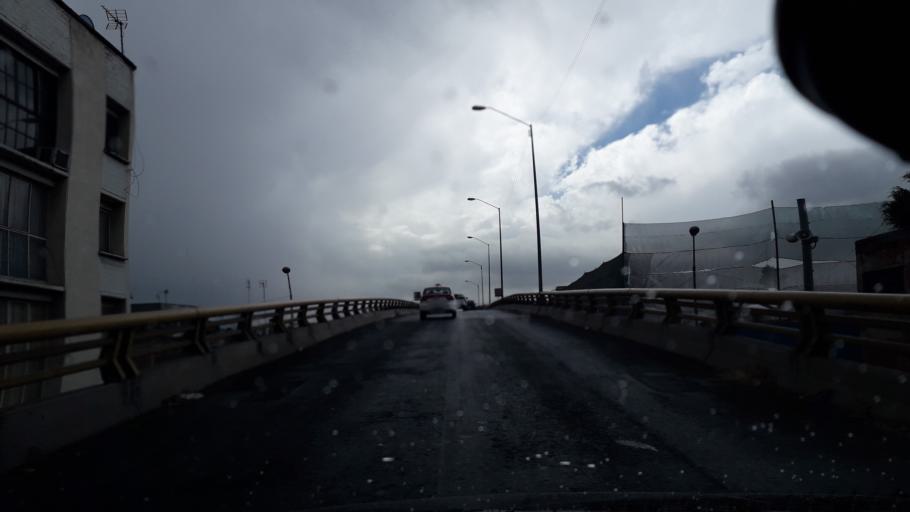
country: MX
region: Mexico City
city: Cuauhtemoc
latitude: 19.4599
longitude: -99.1542
